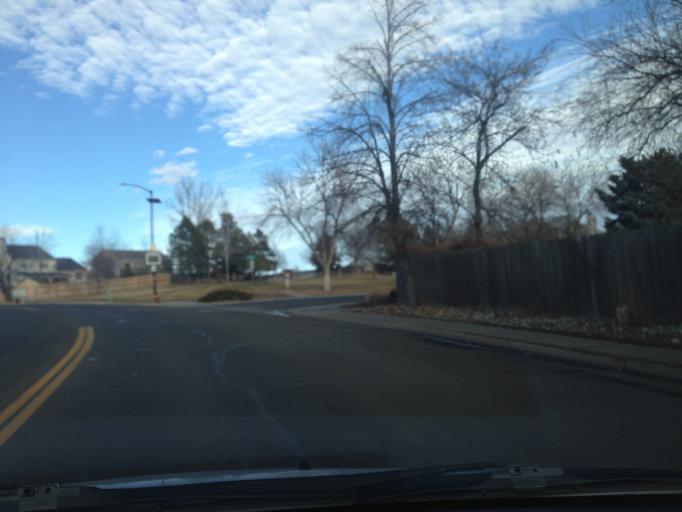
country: US
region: Colorado
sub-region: Boulder County
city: Lafayette
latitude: 39.9975
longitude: -105.1055
